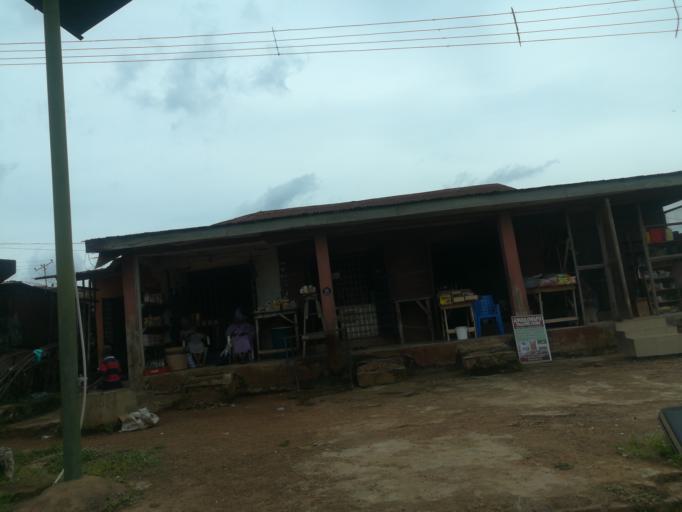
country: NG
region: Oyo
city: Ibadan
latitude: 7.3746
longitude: 3.9617
